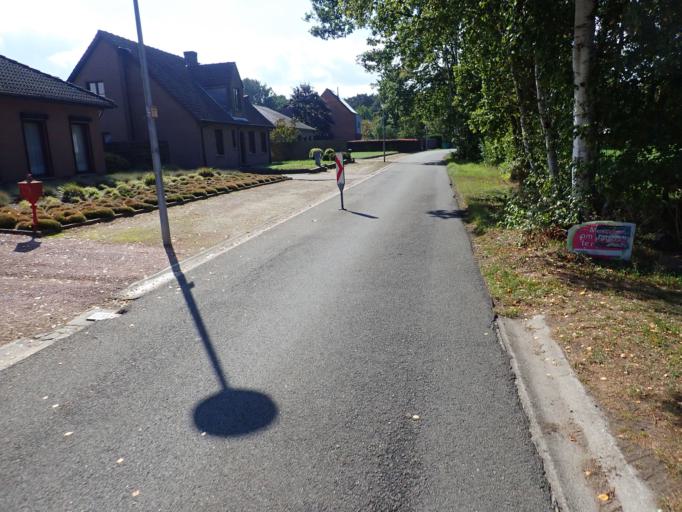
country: BE
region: Flanders
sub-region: Provincie Antwerpen
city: Nijlen
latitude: 51.1649
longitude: 4.6467
